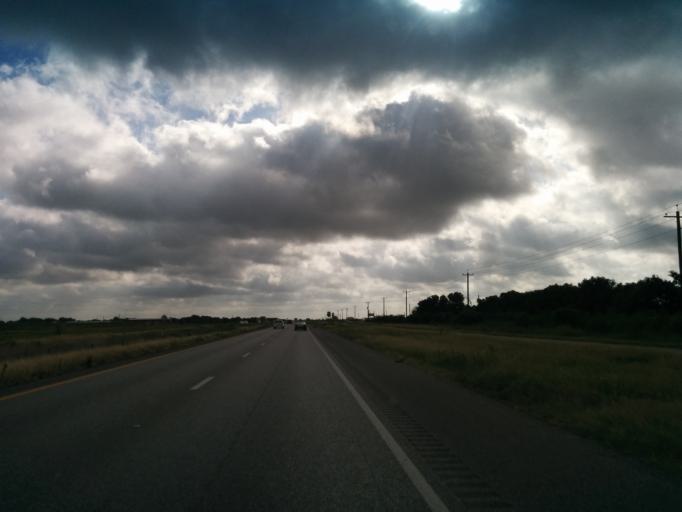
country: US
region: Texas
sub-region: Guadalupe County
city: Marion
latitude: 29.5097
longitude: -98.1633
